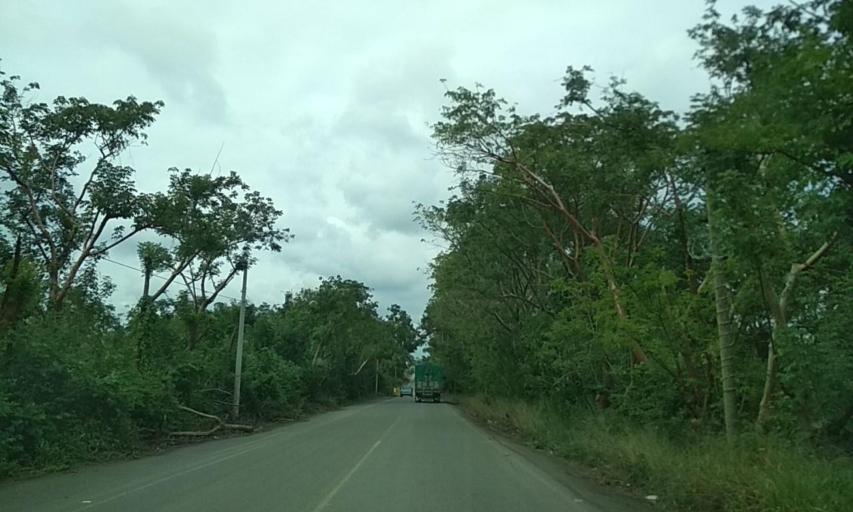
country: MX
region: Veracruz
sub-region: Papantla
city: El Chote
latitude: 20.3688
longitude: -97.3328
